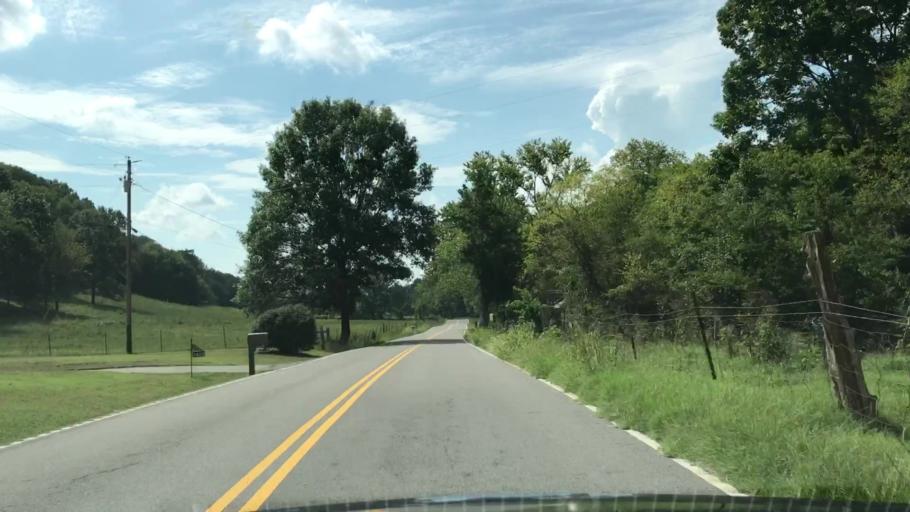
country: US
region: Tennessee
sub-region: Trousdale County
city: Hartsville
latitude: 36.4846
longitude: -86.1879
